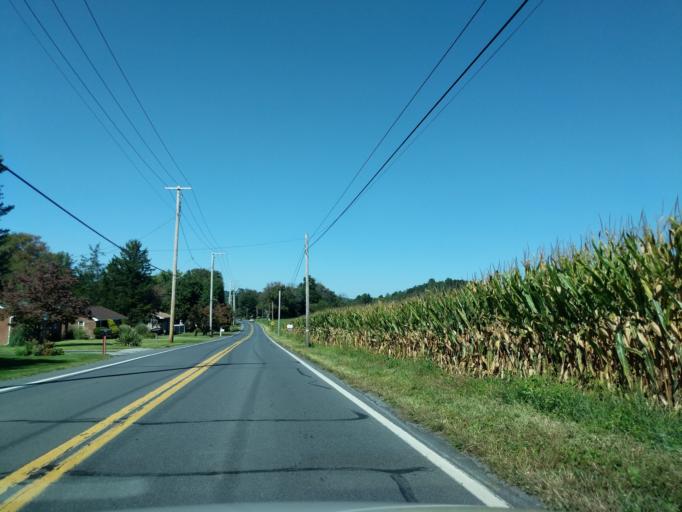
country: US
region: Pennsylvania
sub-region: Lehigh County
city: Coopersburg
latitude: 40.5012
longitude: -75.4438
